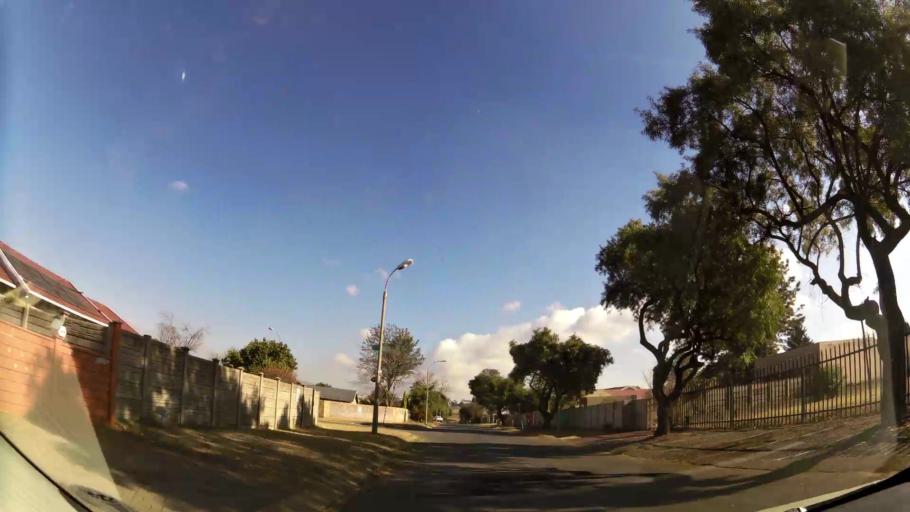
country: ZA
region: Gauteng
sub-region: City of Johannesburg Metropolitan Municipality
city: Roodepoort
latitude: -26.1617
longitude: 27.8195
